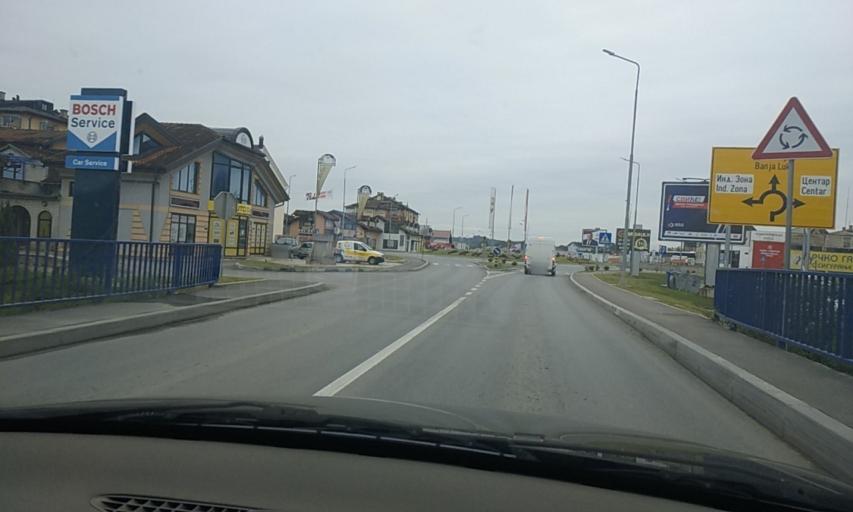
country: BA
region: Republika Srpska
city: Prnjavor
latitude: 44.8665
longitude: 17.6612
